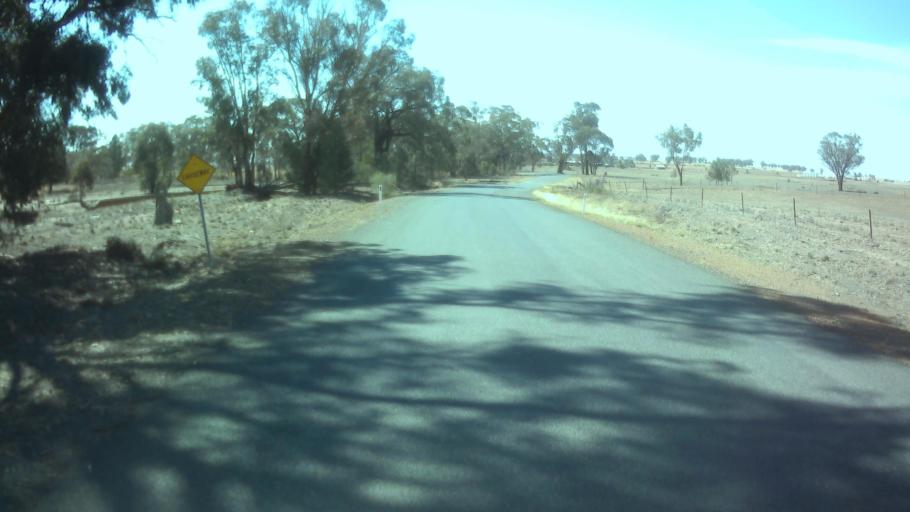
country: AU
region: New South Wales
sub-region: Weddin
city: Grenfell
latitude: -33.7696
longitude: 147.8669
